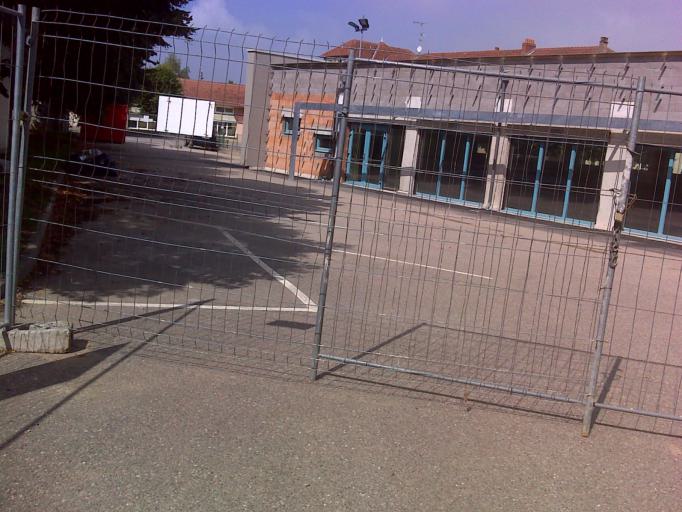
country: FR
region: Lorraine
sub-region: Departement de Meurthe-et-Moselle
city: Damelevieres
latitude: 48.5536
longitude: 6.4064
